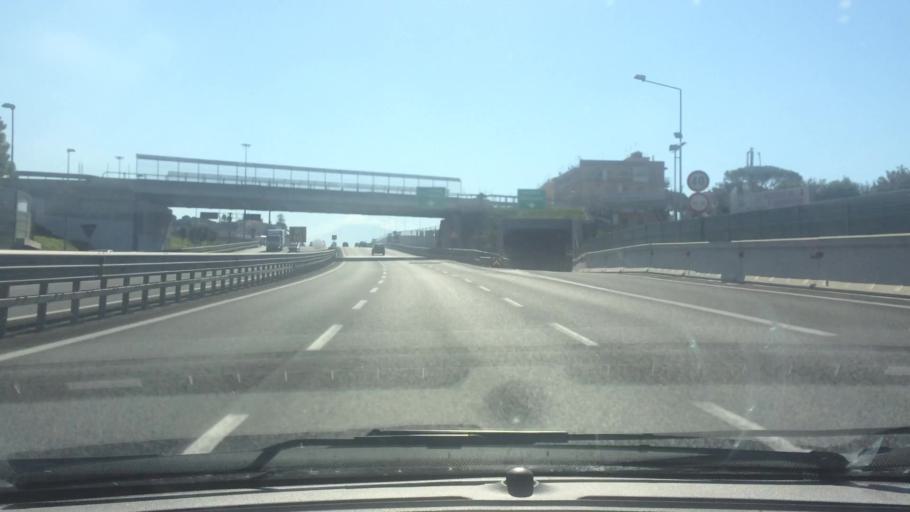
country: IT
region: Campania
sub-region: Provincia di Napoli
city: Ercolano
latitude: 40.8175
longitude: 14.3542
